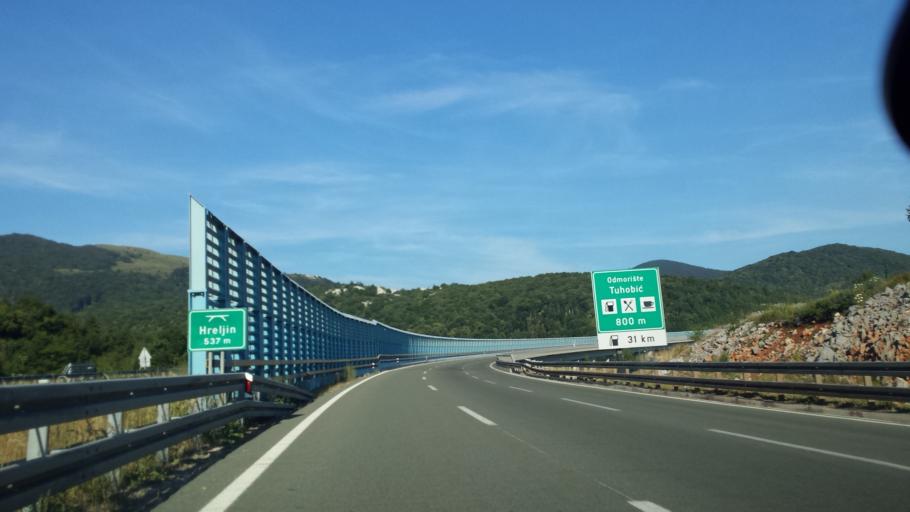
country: HR
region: Primorsko-Goranska
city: Hreljin
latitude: 45.3285
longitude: 14.6126
